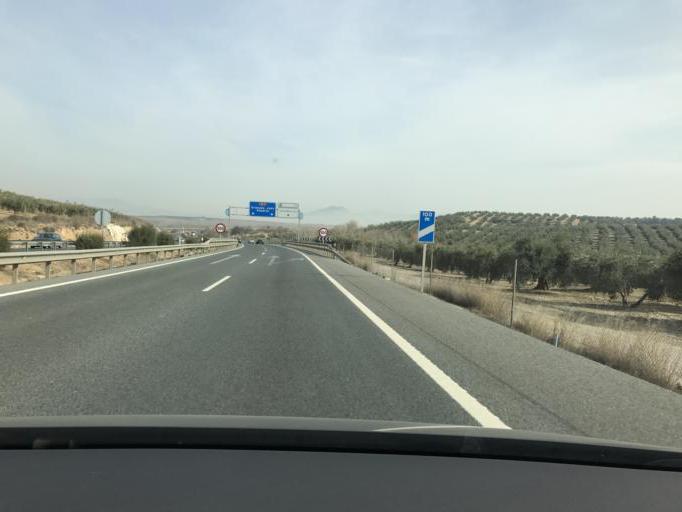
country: ES
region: Andalusia
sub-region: Provincia de Granada
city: Lachar
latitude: 37.1908
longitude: -3.8742
